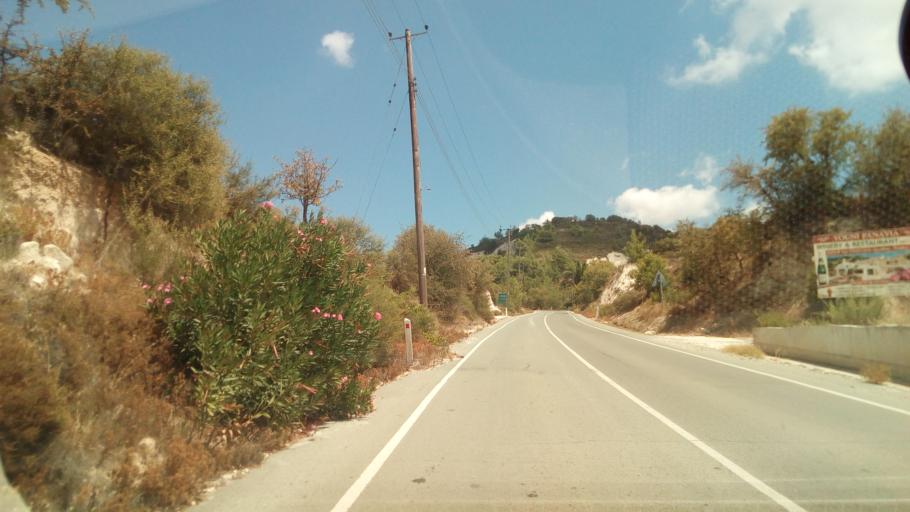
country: CY
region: Pafos
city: Mesogi
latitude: 34.9244
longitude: 32.6215
